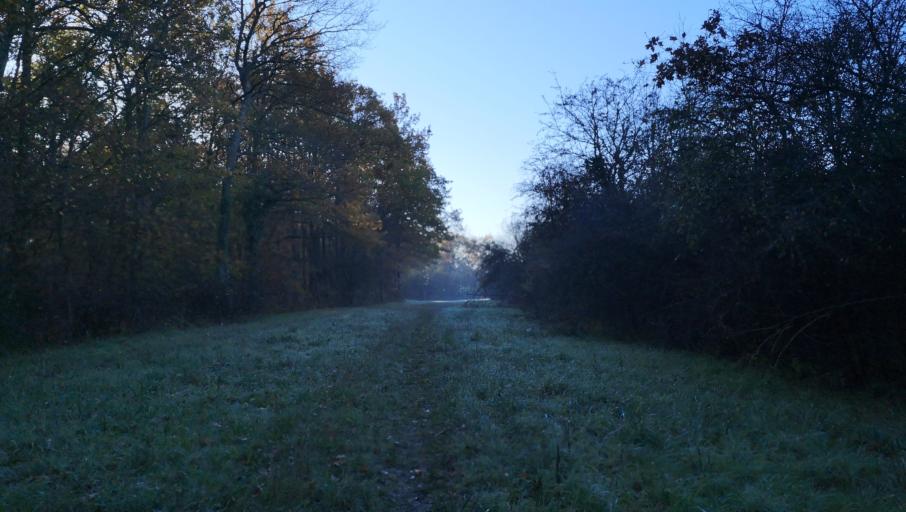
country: FR
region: Centre
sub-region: Departement du Loiret
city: Saran
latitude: 47.9456
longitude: 1.8591
